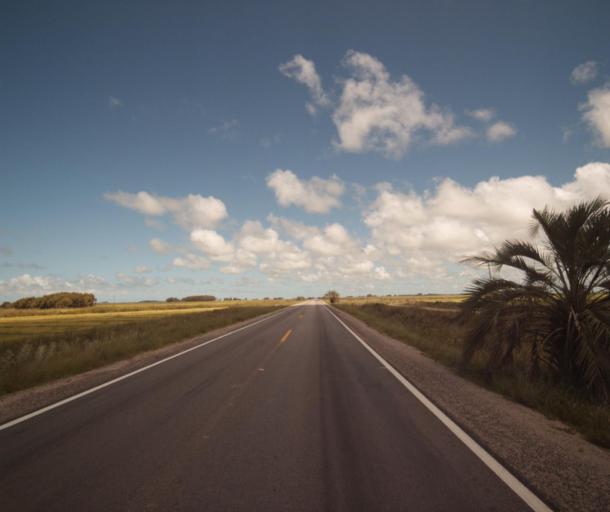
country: UY
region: Cerro Largo
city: Rio Branco
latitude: -32.8955
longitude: -52.7268
